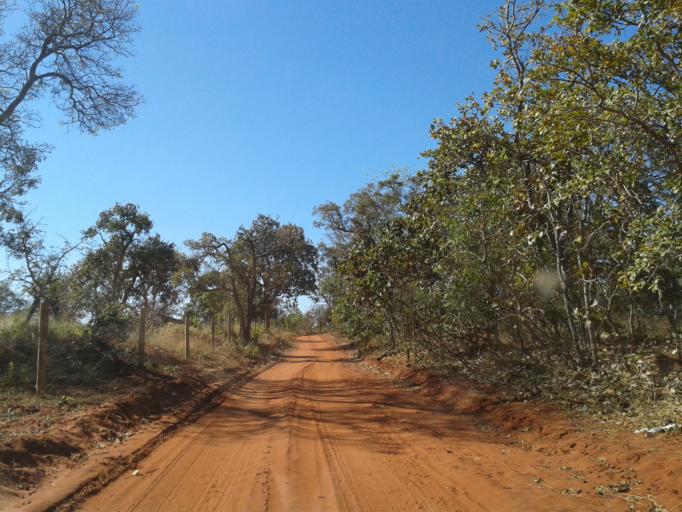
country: BR
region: Minas Gerais
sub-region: Ituiutaba
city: Ituiutaba
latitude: -19.0849
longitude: -49.3369
